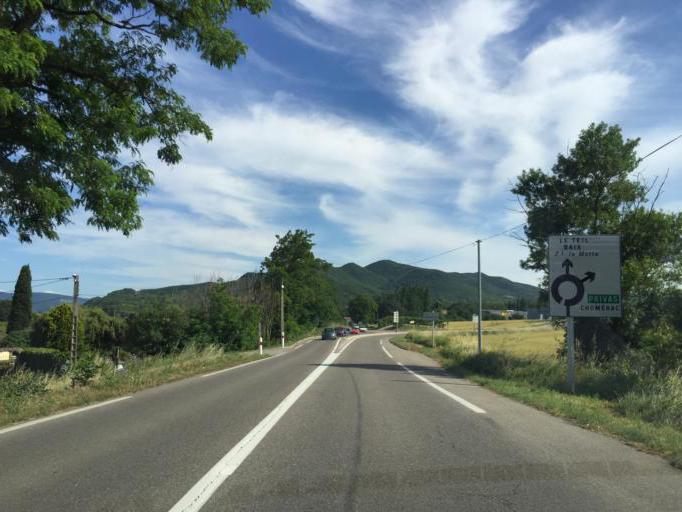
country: FR
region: Rhone-Alpes
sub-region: Departement de l'Ardeche
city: Le Pouzin
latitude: 44.7306
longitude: 4.7402
